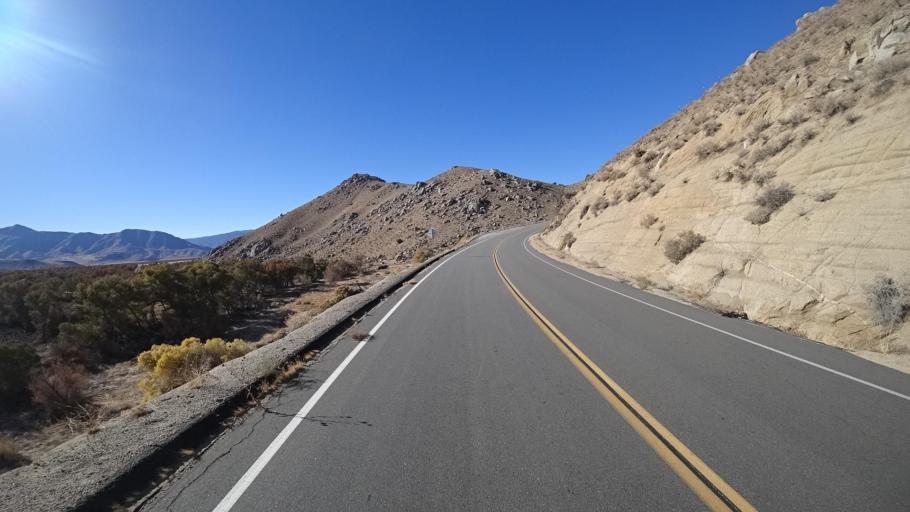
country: US
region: California
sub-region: Kern County
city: Weldon
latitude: 35.6731
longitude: -118.3544
